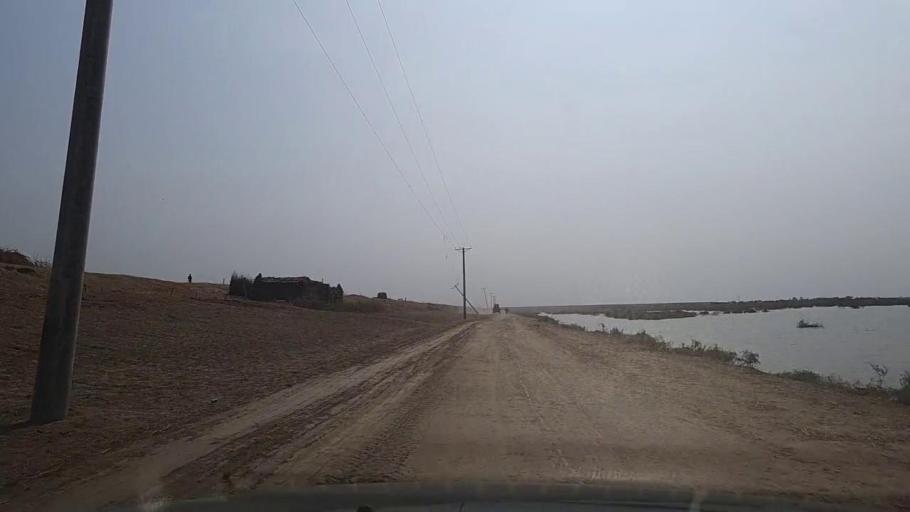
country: PK
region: Sindh
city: Thatta
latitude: 24.5801
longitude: 67.9152
